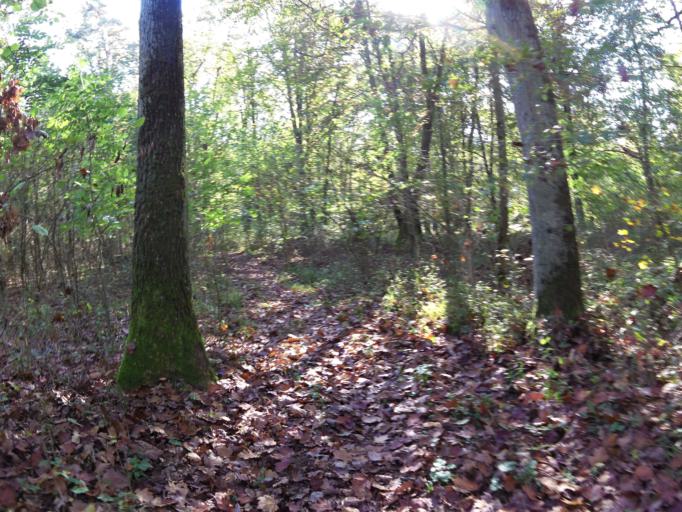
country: DE
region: Bavaria
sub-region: Regierungsbezirk Unterfranken
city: Sulzfeld am Main
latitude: 49.7142
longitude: 10.0965
